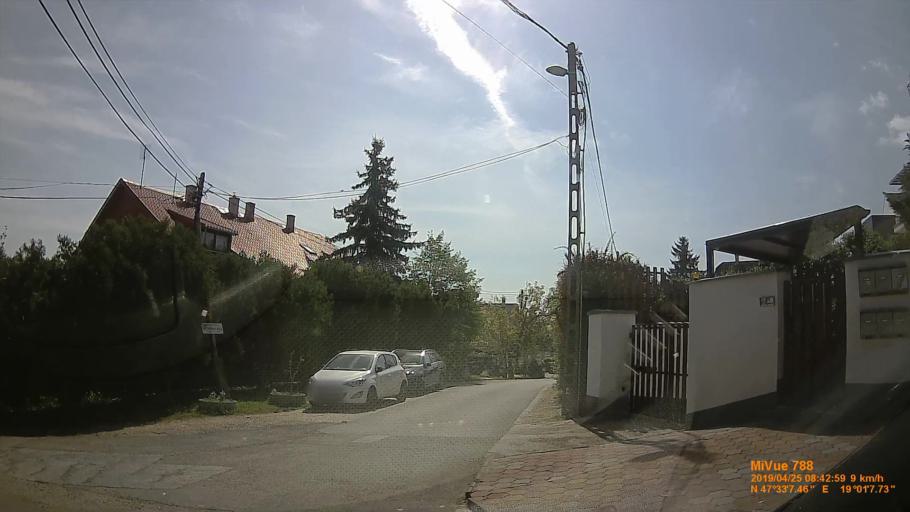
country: HU
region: Budapest
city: Budapest III. keruelet
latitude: 47.5520
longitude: 19.0189
